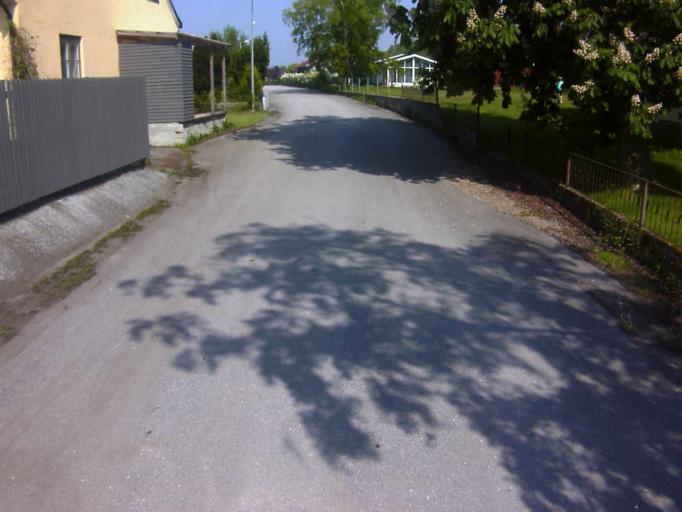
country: SE
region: Blekinge
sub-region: Karlshamns Kommun
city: Morrum
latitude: 56.1175
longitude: 14.6724
